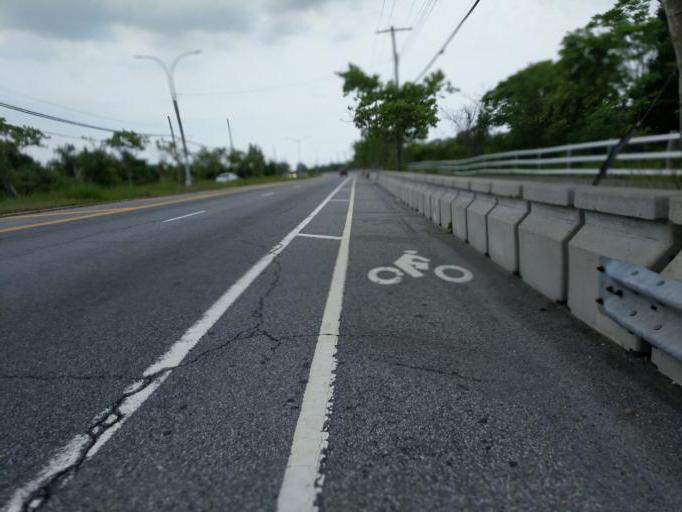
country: US
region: New York
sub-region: Queens County
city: Borough of Queens
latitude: 40.6224
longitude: -73.8263
